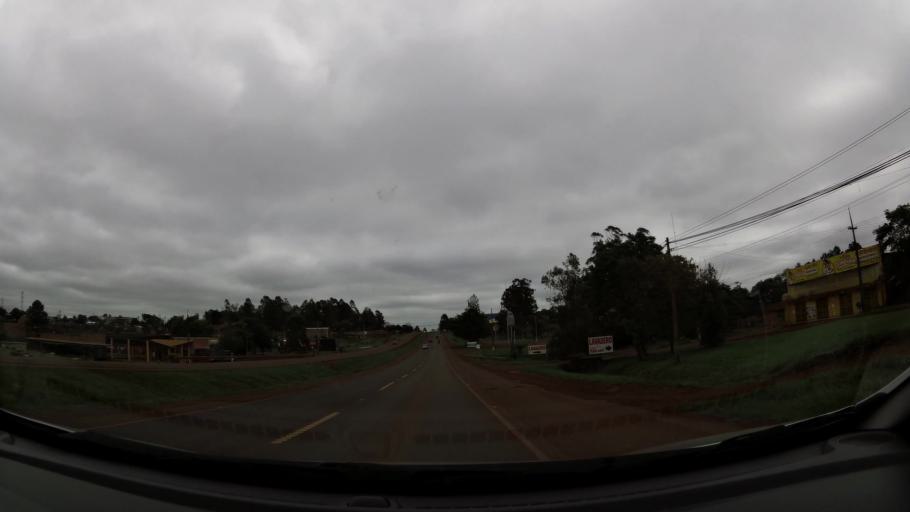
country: PY
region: Alto Parana
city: Presidente Franco
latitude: -25.4894
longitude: -54.7987
